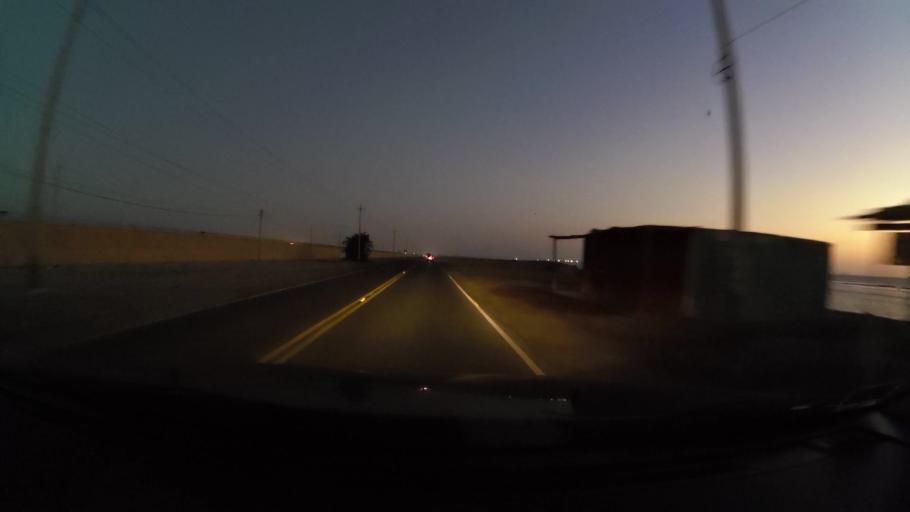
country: PE
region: Ica
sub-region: Provincia de Pisco
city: Pisco
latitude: -13.7483
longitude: -76.2288
